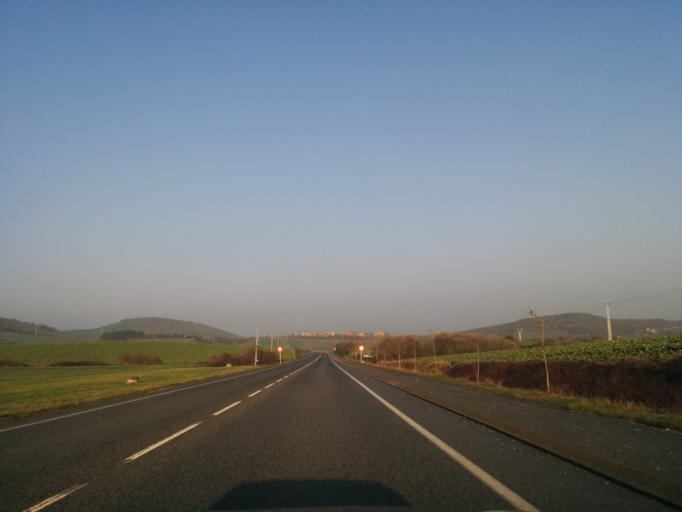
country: ES
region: Navarre
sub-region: Provincia de Navarra
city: Elorz
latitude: 42.7638
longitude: -1.5679
